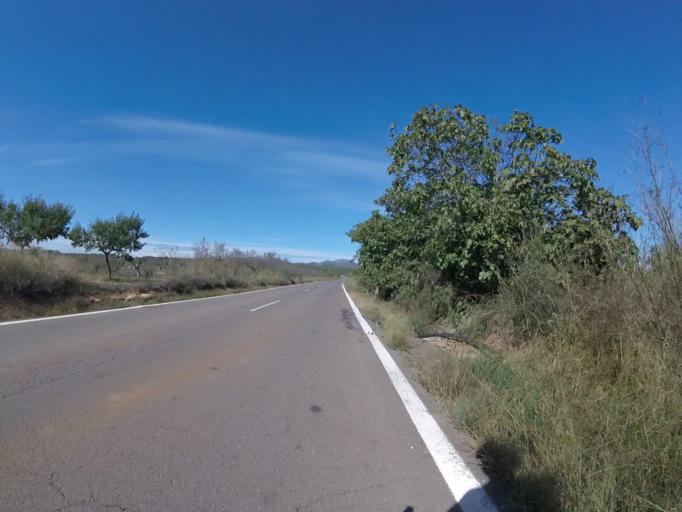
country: ES
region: Valencia
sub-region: Provincia de Castello
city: Benlloch
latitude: 40.2154
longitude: 0.0197
